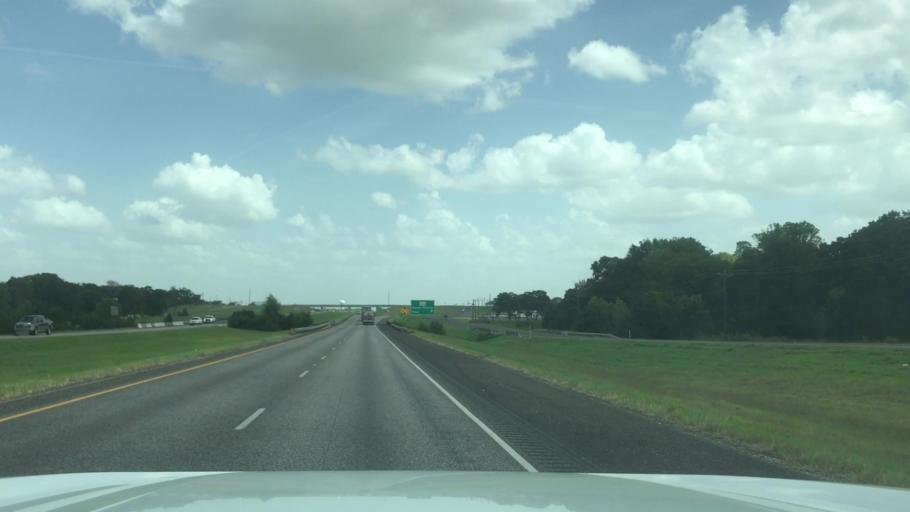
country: US
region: Texas
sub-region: Brazos County
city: Bryan
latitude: 30.7331
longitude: -96.4332
